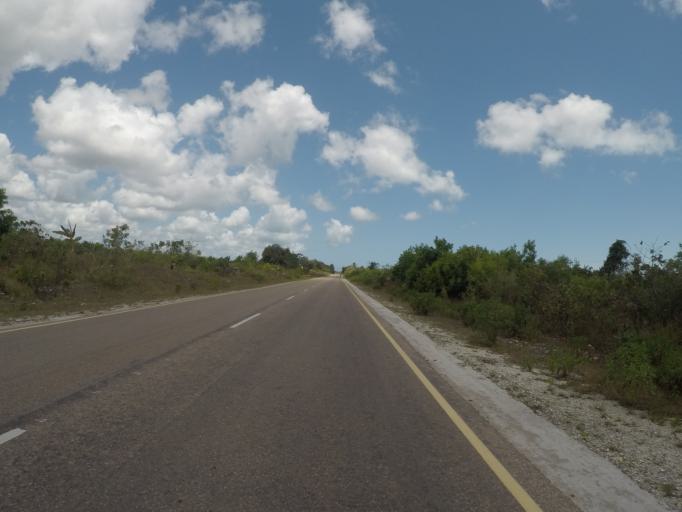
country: TZ
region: Zanzibar Central/South
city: Koani
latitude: -6.2628
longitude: 39.3598
